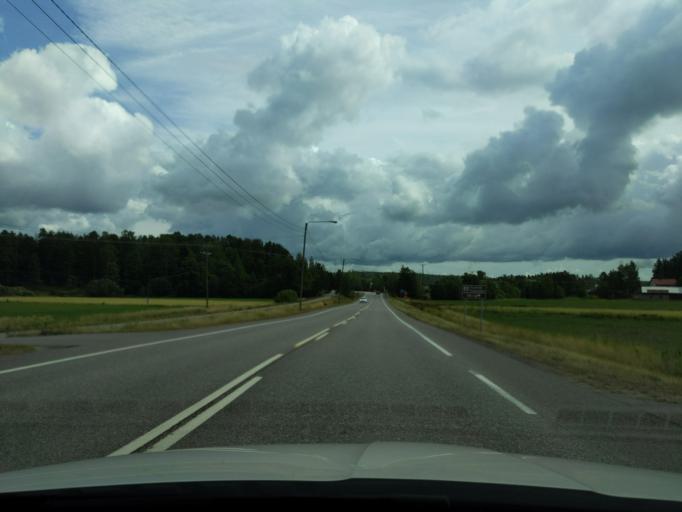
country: FI
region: Uusimaa
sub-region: Porvoo
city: Porvoo
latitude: 60.4549
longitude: 25.7436
